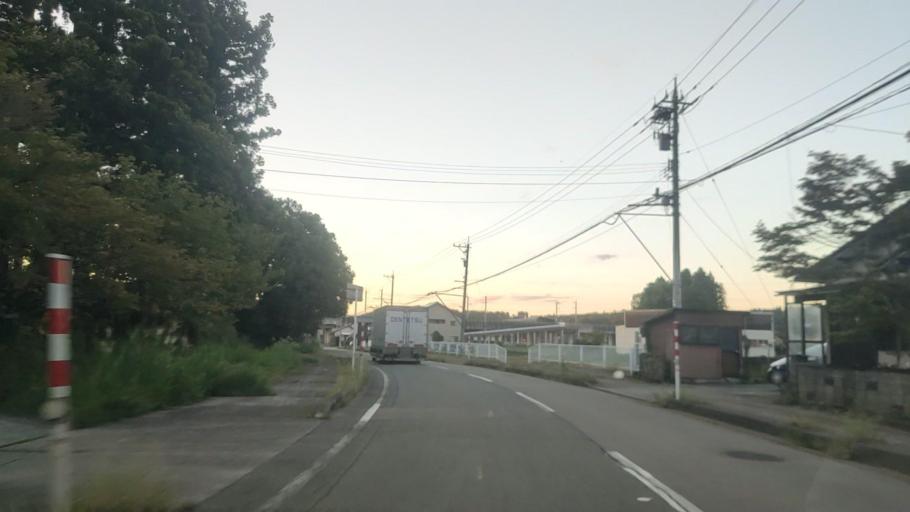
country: JP
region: Ishikawa
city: Tsubata
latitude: 36.6597
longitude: 136.7535
